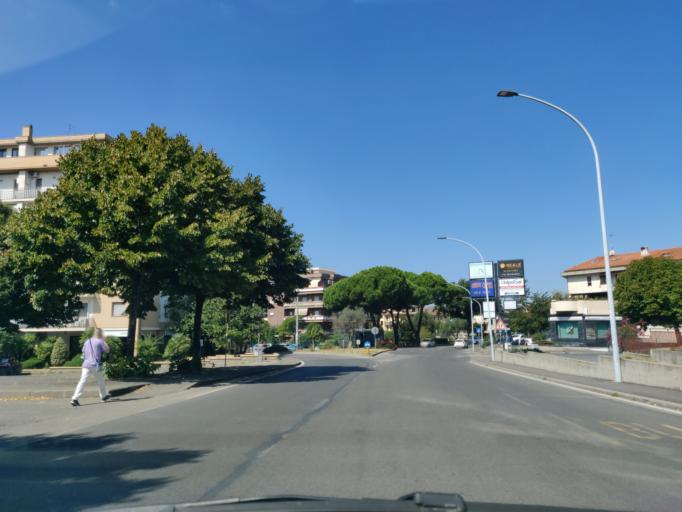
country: IT
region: Latium
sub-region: Provincia di Viterbo
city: Viterbo
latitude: 42.4273
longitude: 12.1017
